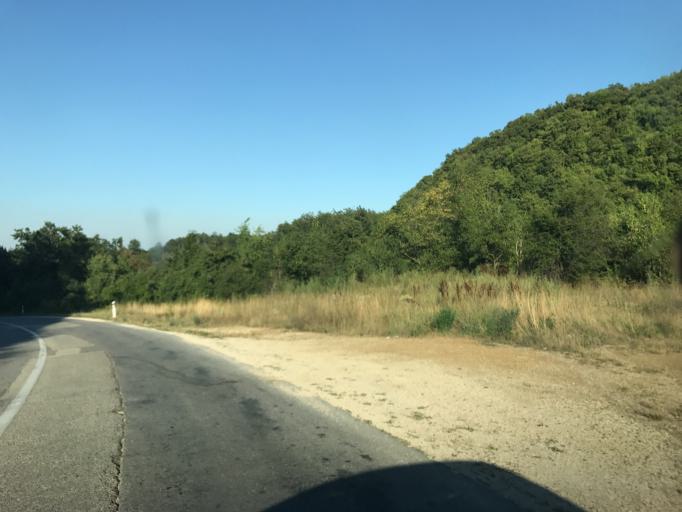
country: RO
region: Mehedinti
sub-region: Comuna Gogosu
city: Ostrovu Mare
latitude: 44.2850
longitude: 22.3184
